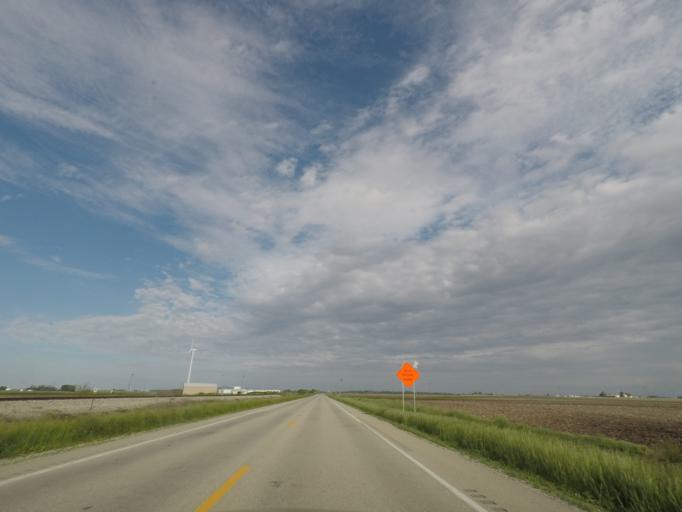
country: US
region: Illinois
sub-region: Logan County
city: Mount Pulaski
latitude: 39.9920
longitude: -89.2447
